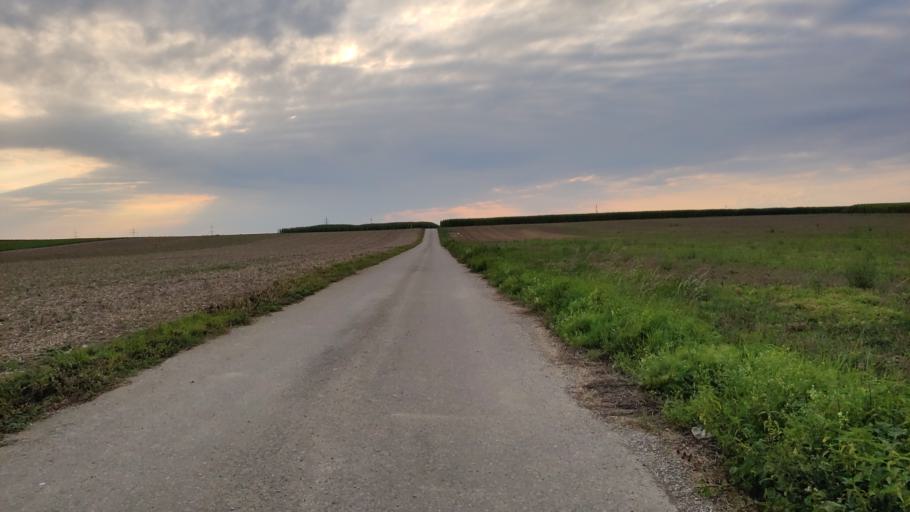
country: DE
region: Bavaria
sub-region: Swabia
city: Oberottmarshausen
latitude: 48.2485
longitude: 10.8652
